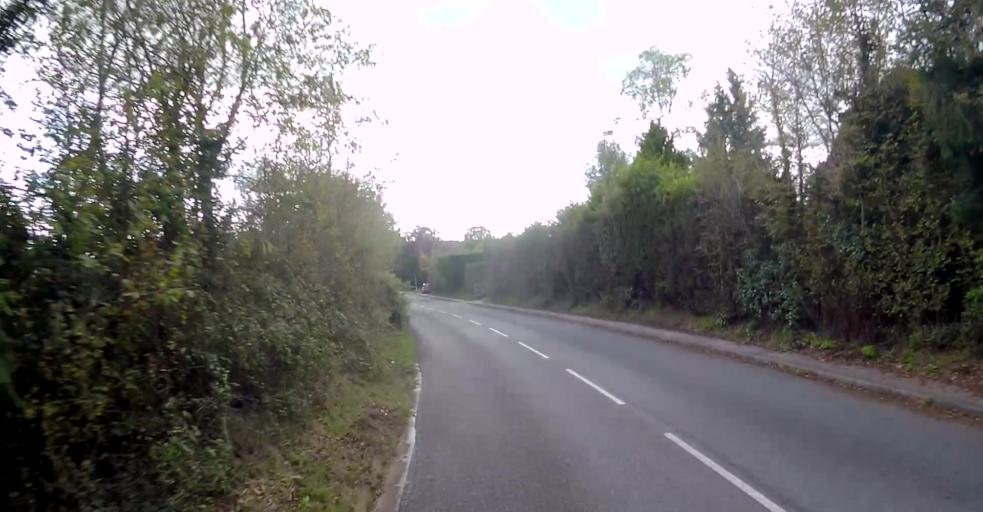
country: GB
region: England
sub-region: Surrey
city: Elstead
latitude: 51.1888
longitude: -0.7477
